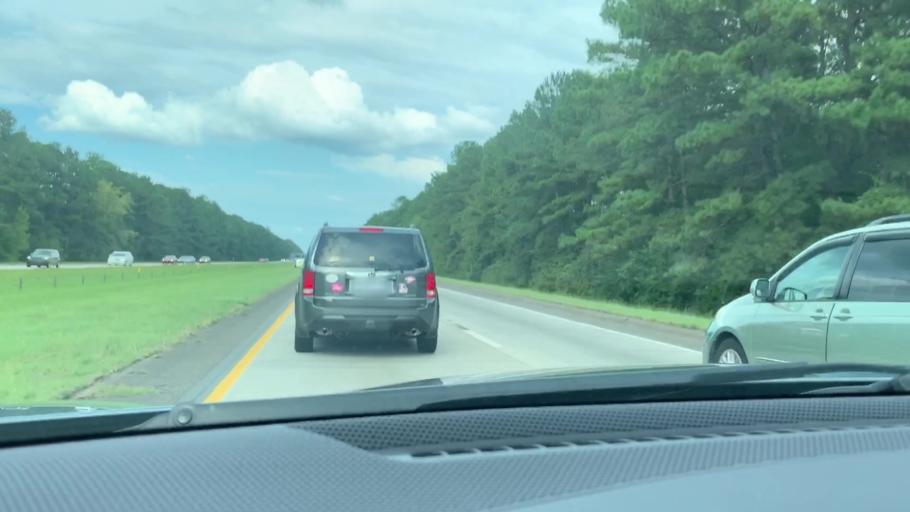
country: US
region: South Carolina
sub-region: Colleton County
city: Walterboro
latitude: 32.8319
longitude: -80.7452
